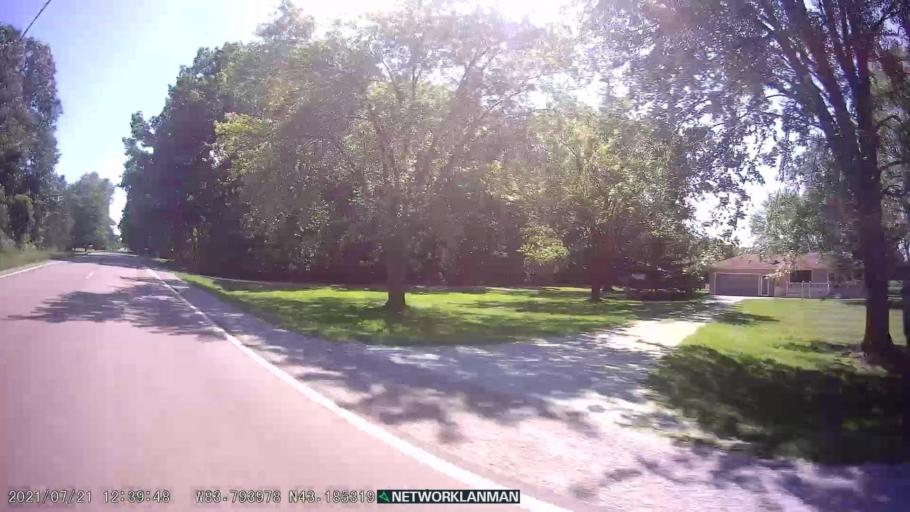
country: US
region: Michigan
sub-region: Genesee County
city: Clio
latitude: 43.1852
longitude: -83.7928
